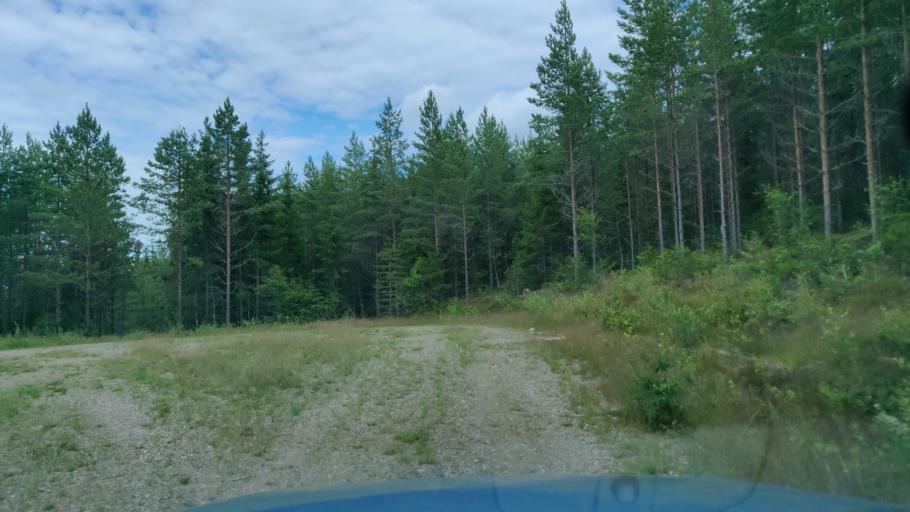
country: SE
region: Vaermland
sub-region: Hagfors Kommun
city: Hagfors
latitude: 59.9699
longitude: 13.5828
